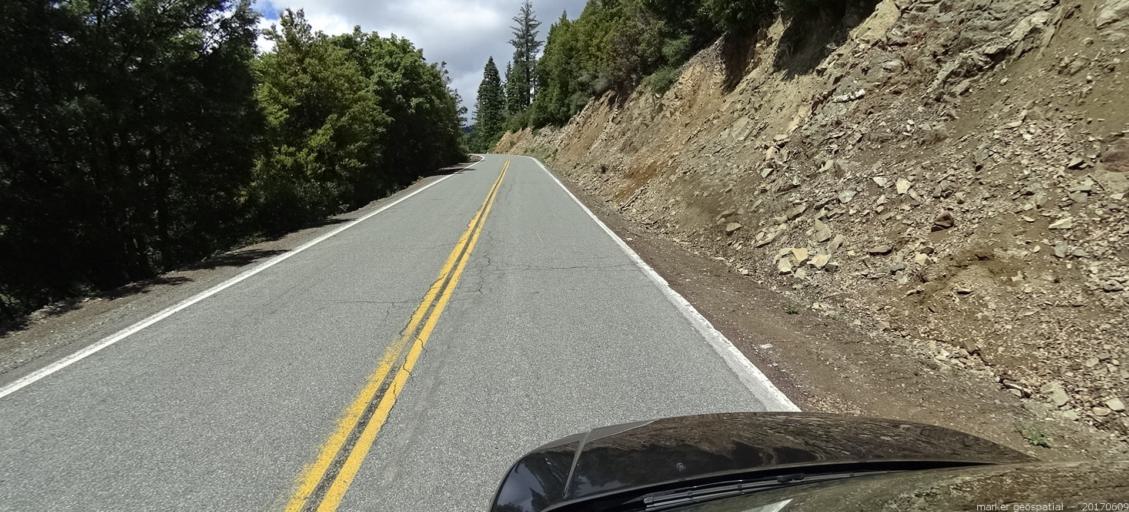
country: US
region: California
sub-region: Siskiyou County
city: Yreka
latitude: 41.3742
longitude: -123.0120
